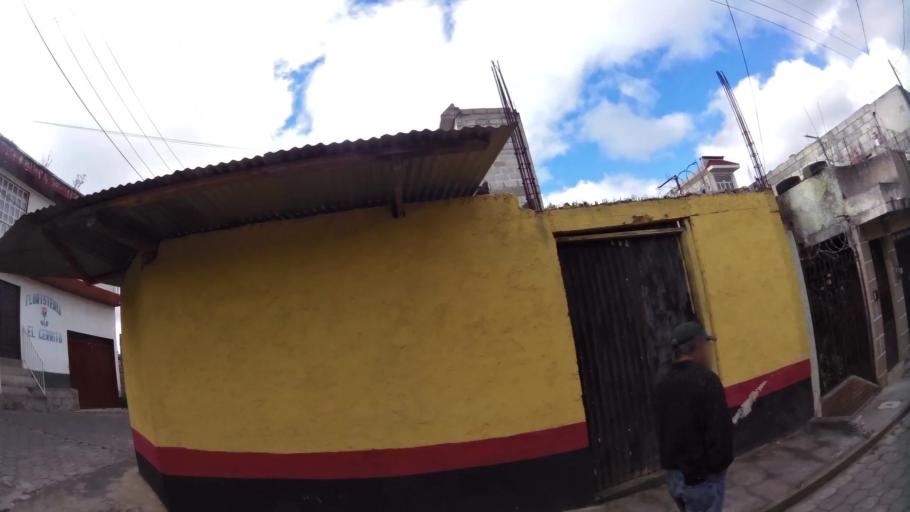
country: GT
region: Quetzaltenango
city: Salcaja
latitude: 14.8793
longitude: -91.4522
